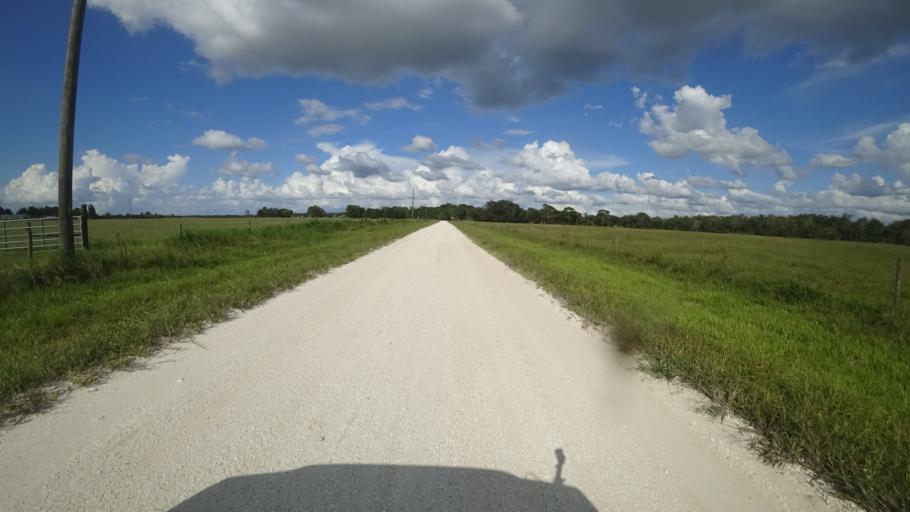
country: US
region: Florida
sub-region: Sarasota County
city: Lake Sarasota
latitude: 27.3371
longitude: -82.1776
